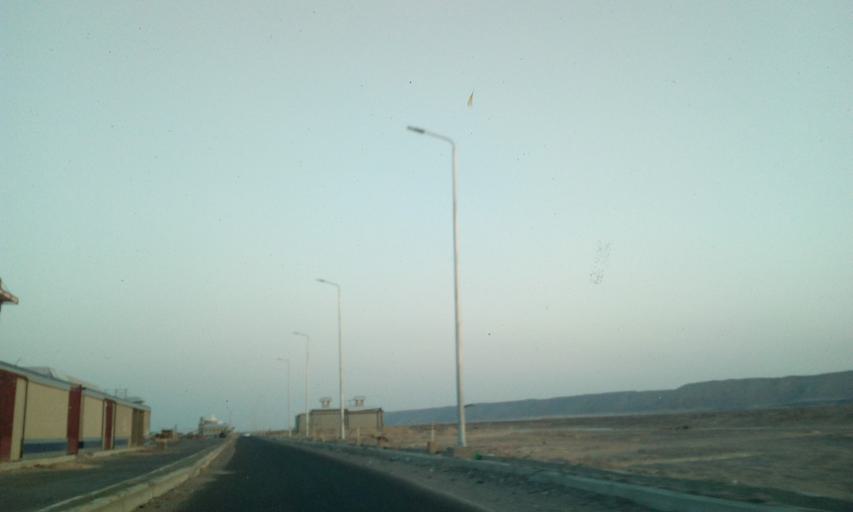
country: EG
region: Red Sea
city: El Gouna
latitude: 27.4313
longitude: 33.6083
